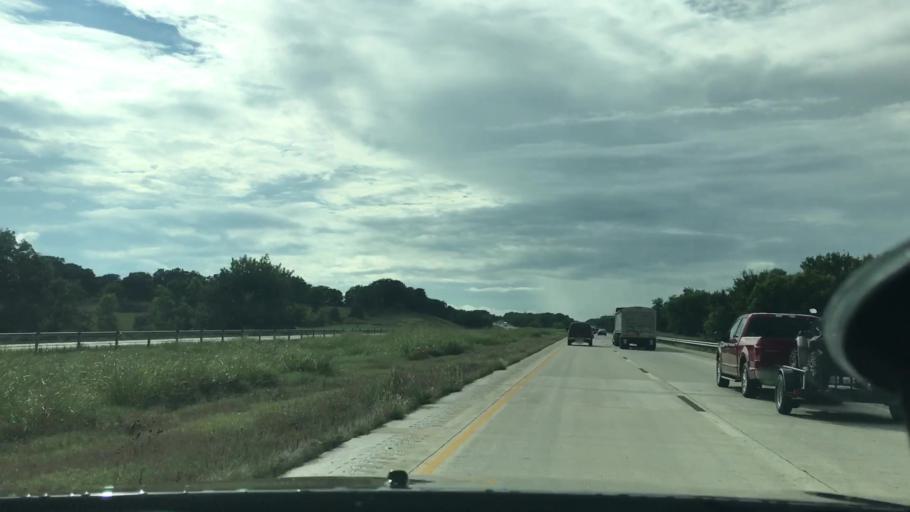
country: US
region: Oklahoma
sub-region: Okfuskee County
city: Boley
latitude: 35.3817
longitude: -96.5483
